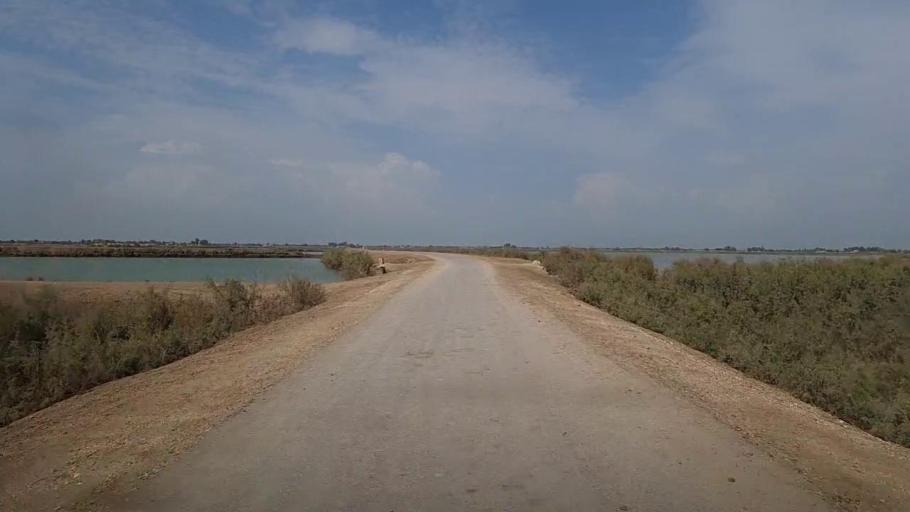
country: PK
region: Sindh
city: Thul
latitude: 28.2774
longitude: 68.8213
